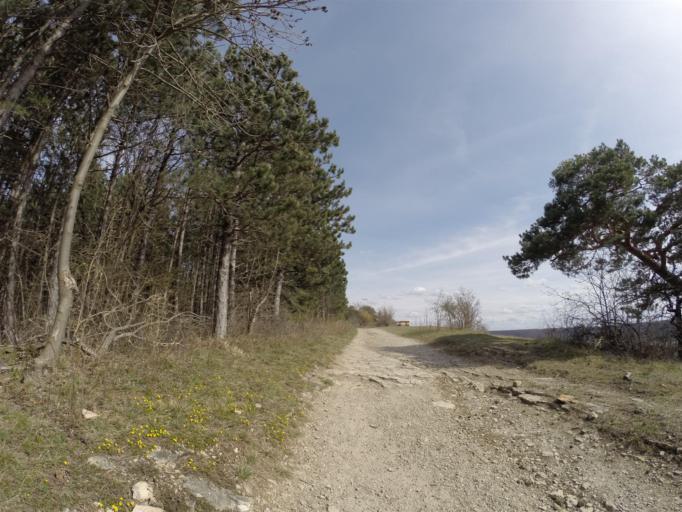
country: DE
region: Thuringia
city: Golmsdorf
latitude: 50.9391
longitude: 11.6328
